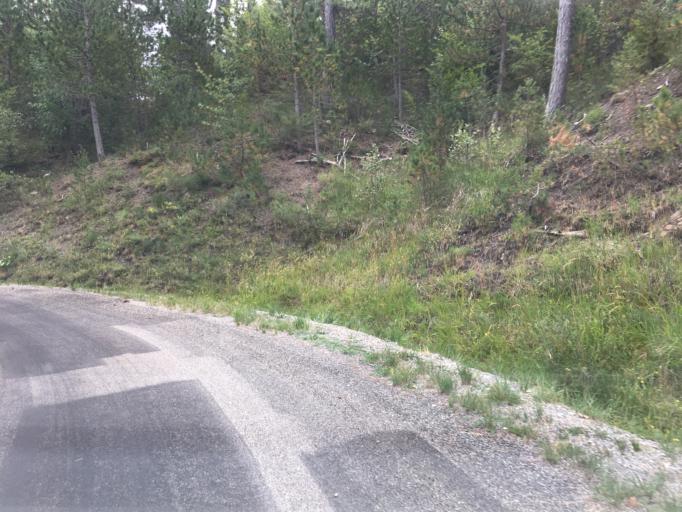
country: FR
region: Provence-Alpes-Cote d'Azur
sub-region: Departement des Alpes-de-Haute-Provence
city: Digne-les-Bains
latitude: 44.2159
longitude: 6.1443
